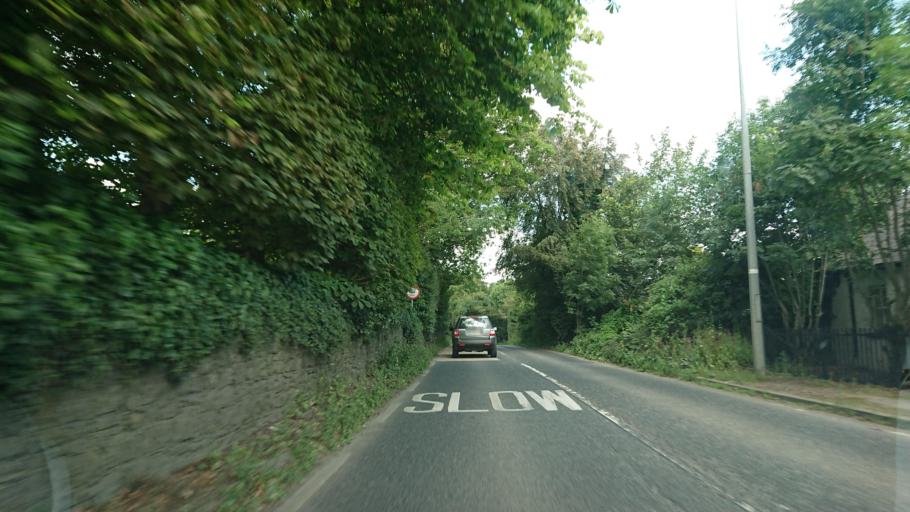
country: IE
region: Leinster
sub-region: Kildare
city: Sallins
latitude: 53.2667
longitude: -6.6705
